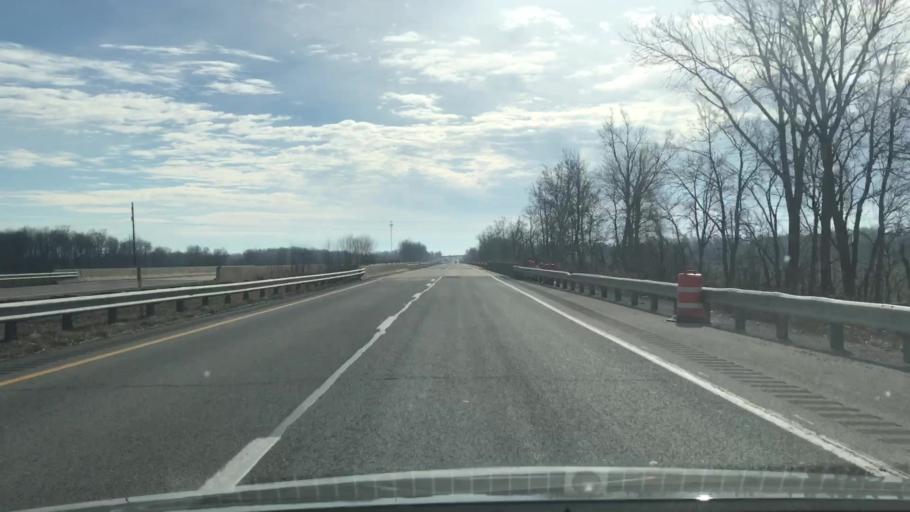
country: US
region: Kentucky
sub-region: Daviess County
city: Masonville
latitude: 37.7127
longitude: -87.0479
